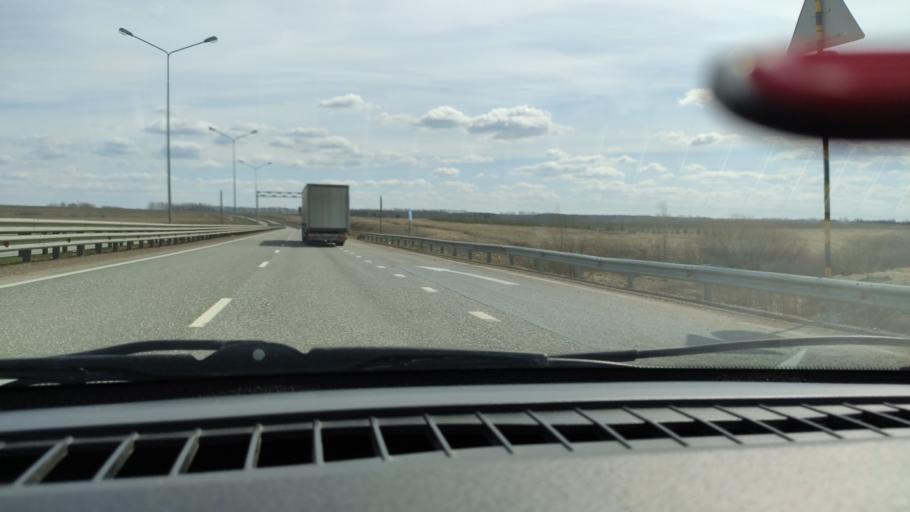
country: RU
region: Bashkortostan
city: Kushnarenkovo
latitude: 55.0675
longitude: 55.2998
